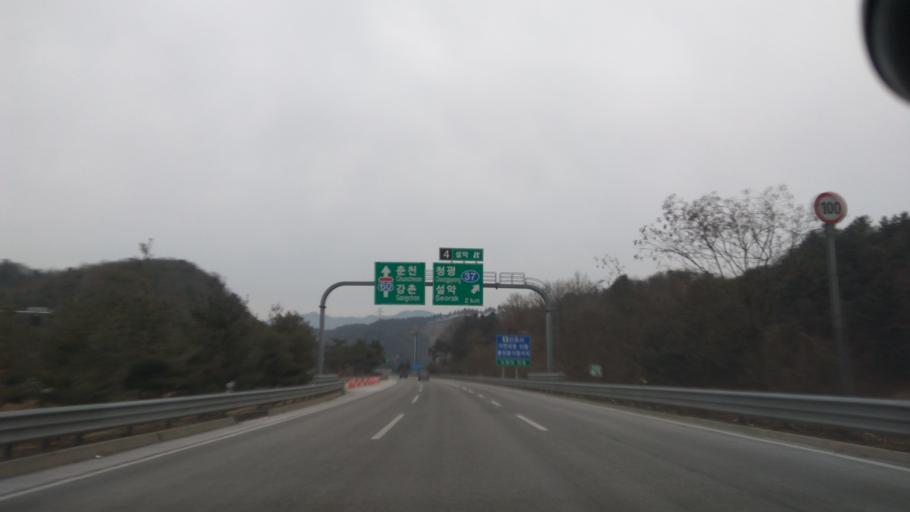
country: KR
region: Gyeonggi-do
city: Cheongpyeong
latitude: 37.6514
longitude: 127.4805
